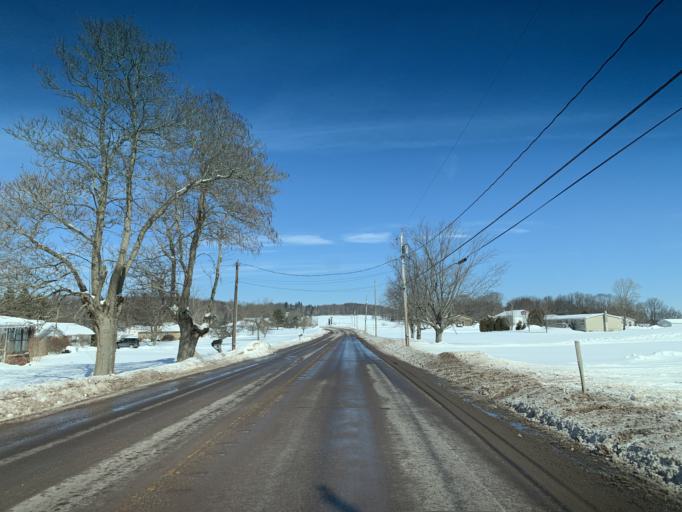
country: US
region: Pennsylvania
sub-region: Somerset County
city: Meyersdale
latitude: 39.7149
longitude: -79.1600
